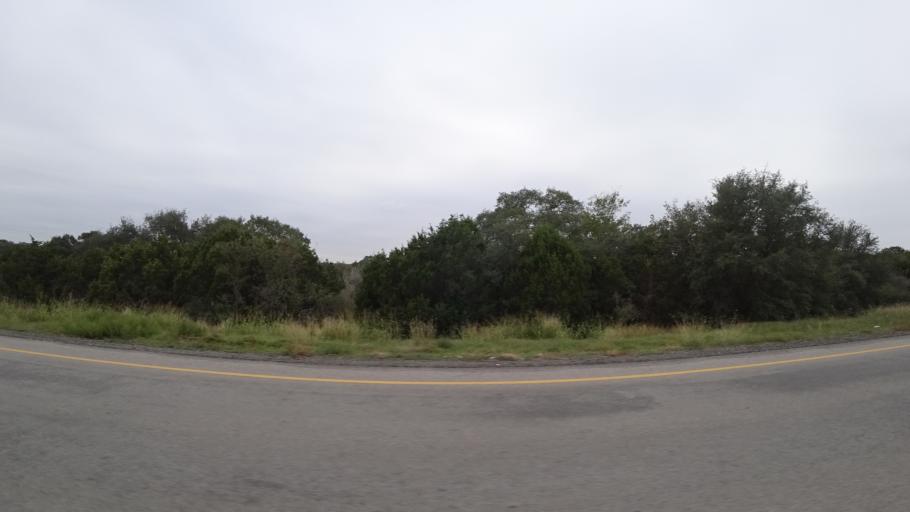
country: US
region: Texas
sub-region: Travis County
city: Shady Hollow
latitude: 30.1839
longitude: -97.9045
